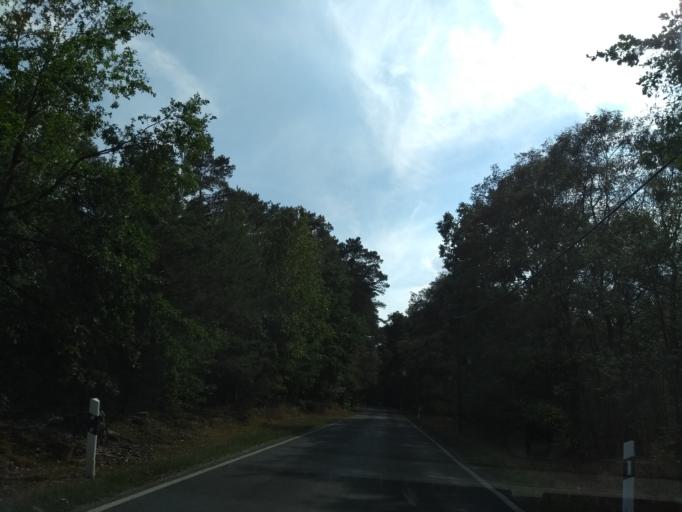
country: DE
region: Brandenburg
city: Luebben
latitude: 51.8607
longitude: 13.8504
